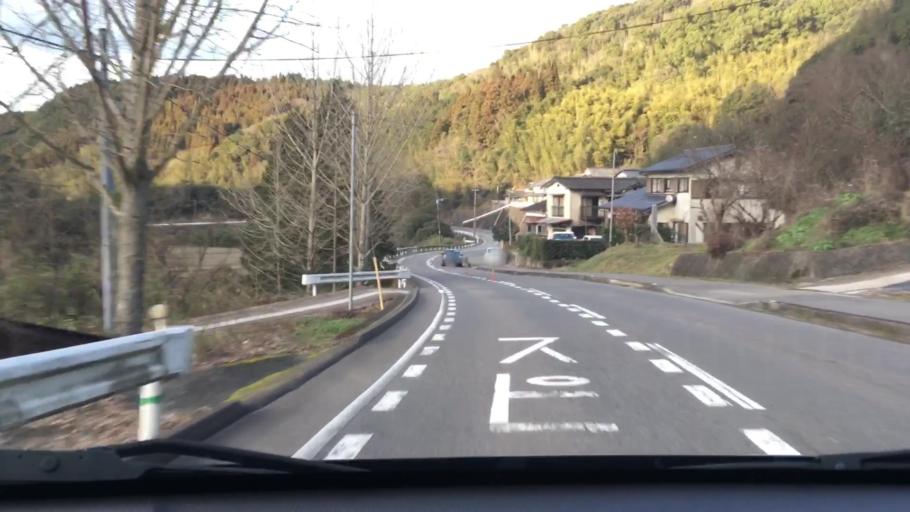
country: JP
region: Oita
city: Hiji
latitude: 33.4178
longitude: 131.4191
